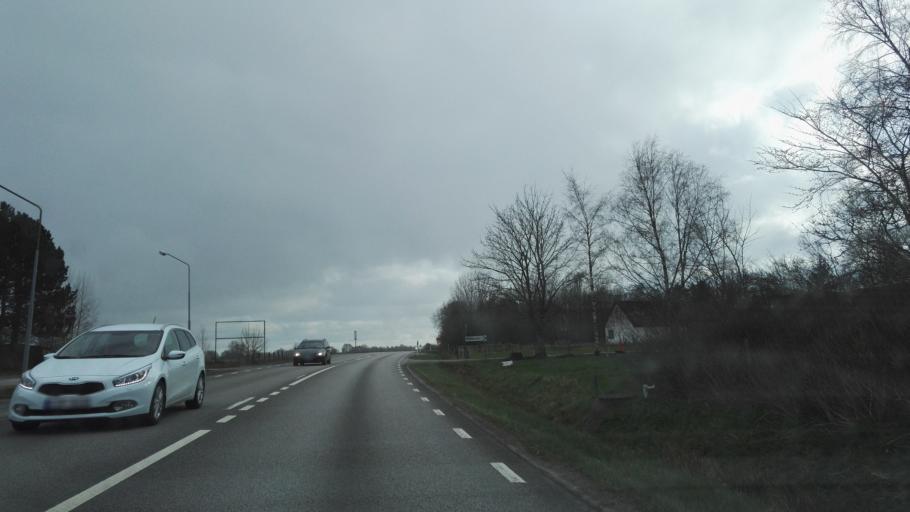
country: SE
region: Skane
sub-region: Horby Kommun
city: Hoerby
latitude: 55.7841
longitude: 13.6772
